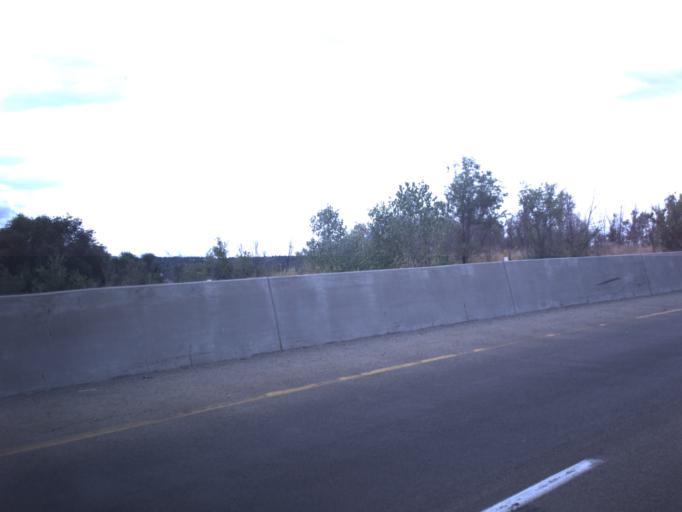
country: US
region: Utah
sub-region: Weber County
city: Ogden
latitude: 41.2084
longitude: -111.9825
